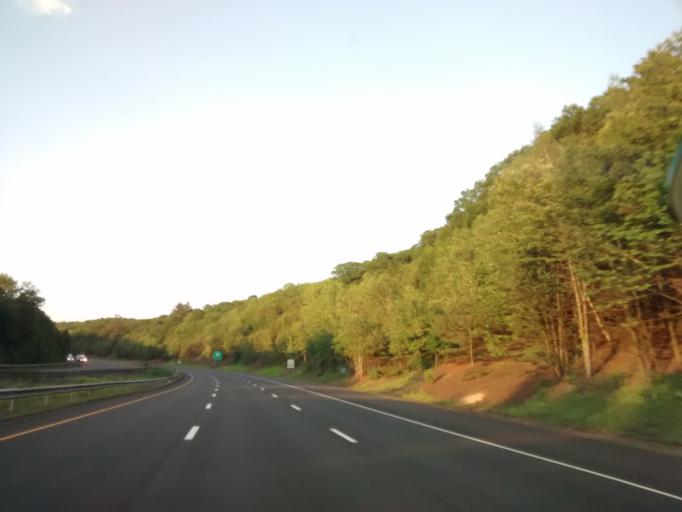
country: US
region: Connecticut
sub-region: Tolland County
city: Stafford Springs
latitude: 41.9034
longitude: -72.2798
